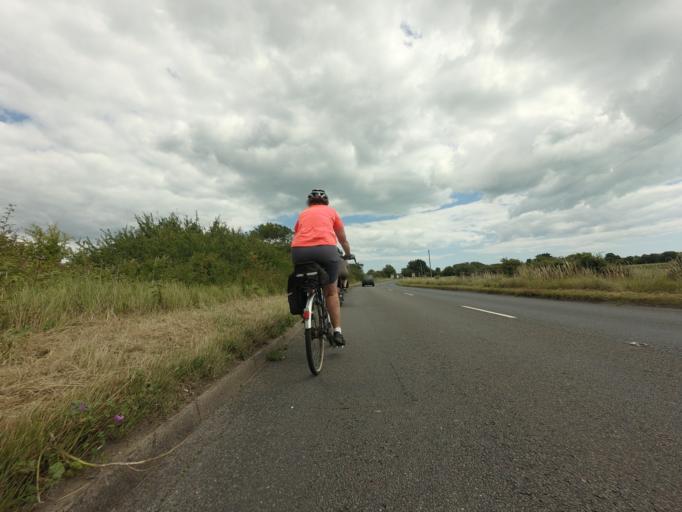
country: GB
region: England
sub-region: East Sussex
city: Pevensey
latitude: 50.8164
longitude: 0.3475
